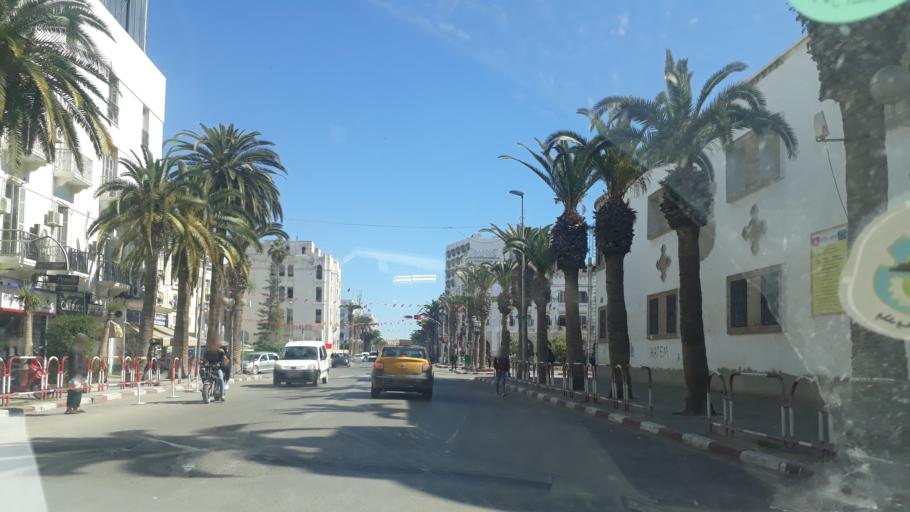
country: TN
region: Safaqis
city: Sfax
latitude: 34.7318
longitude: 10.7629
